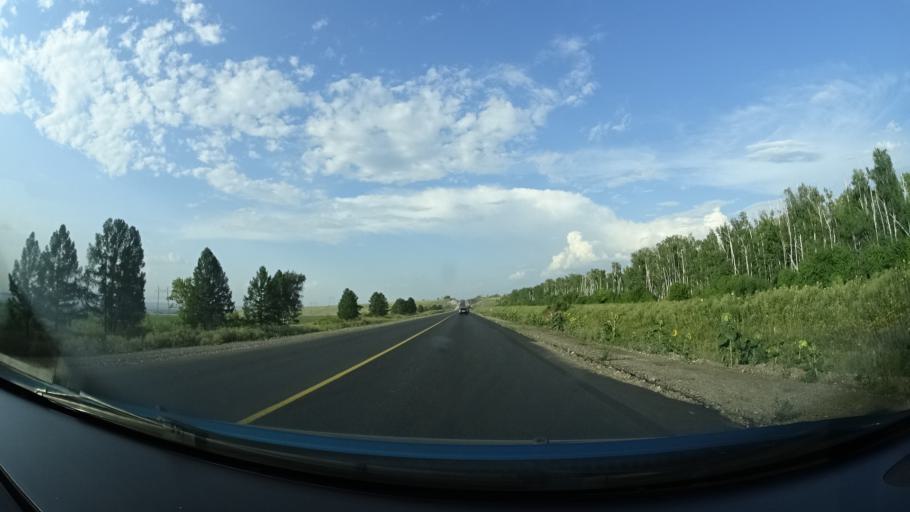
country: RU
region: Samara
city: Sukhodol
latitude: 53.7241
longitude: 50.8321
